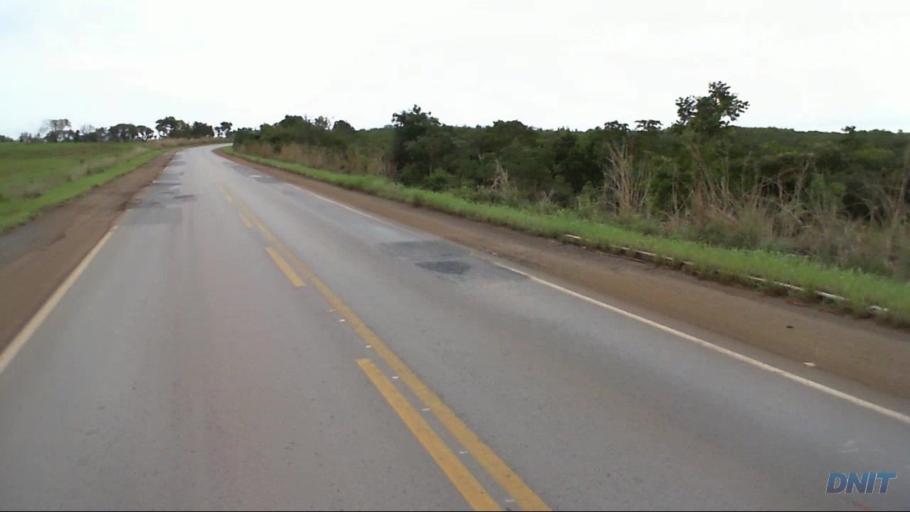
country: BR
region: Goias
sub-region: Barro Alto
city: Barro Alto
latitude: -14.7919
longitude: -49.0528
